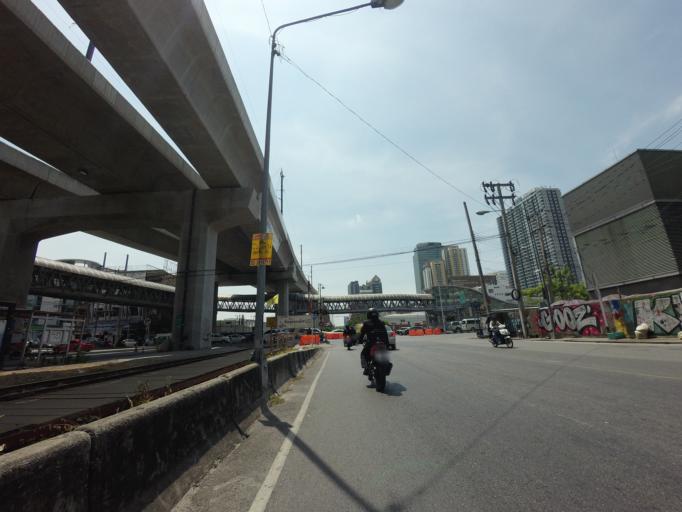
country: TH
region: Bangkok
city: Din Daeng
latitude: 13.7502
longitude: 100.5633
